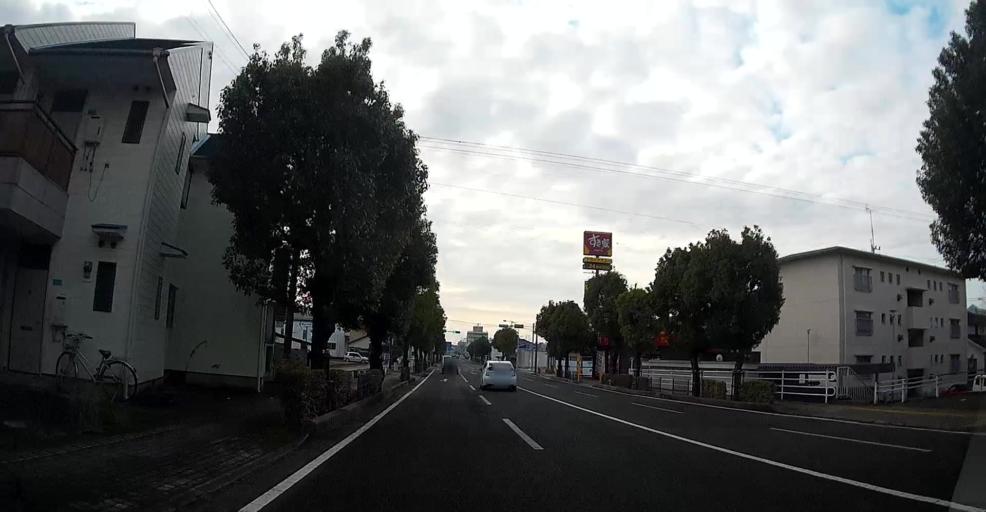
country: JP
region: Kumamoto
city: Hondo
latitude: 32.4622
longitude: 130.1911
